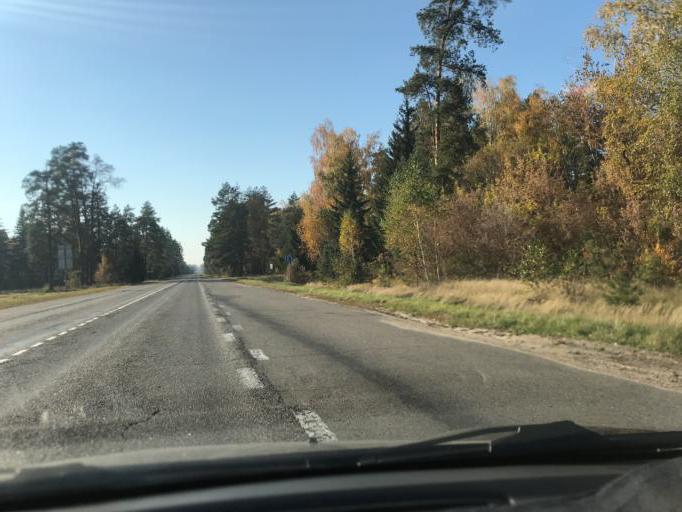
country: BY
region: Mogilev
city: Hlusha
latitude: 53.0865
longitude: 28.8441
